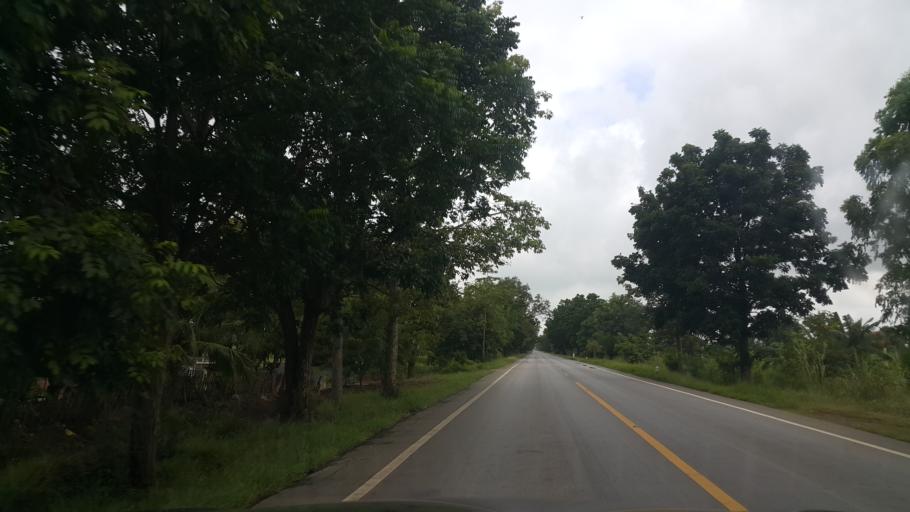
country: TH
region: Sukhothai
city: Sawankhalok
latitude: 17.3718
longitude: 99.7409
